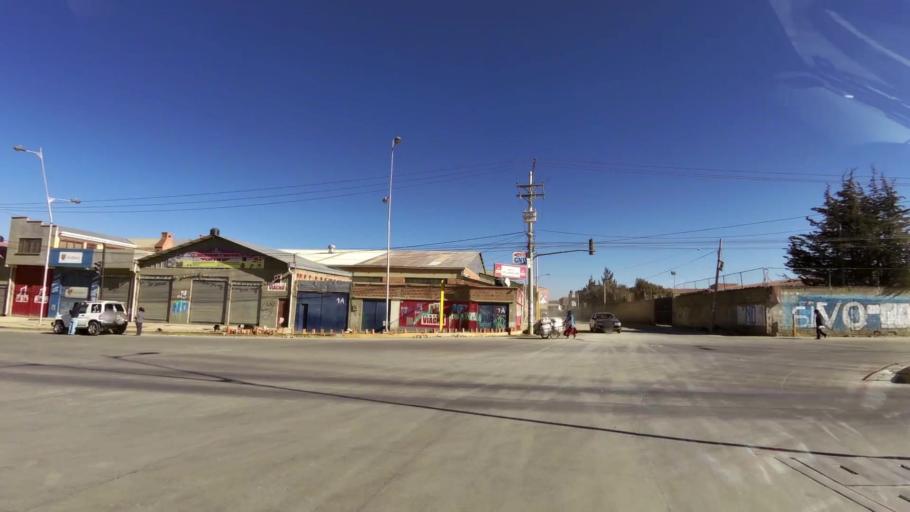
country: BO
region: La Paz
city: La Paz
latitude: -16.5213
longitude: -68.1785
